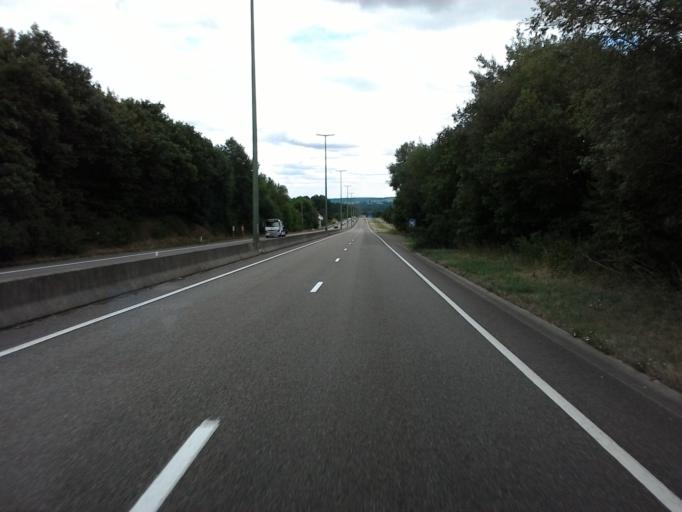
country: BE
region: Wallonia
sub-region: Province du Luxembourg
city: Attert
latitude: 49.7718
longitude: 5.7618
